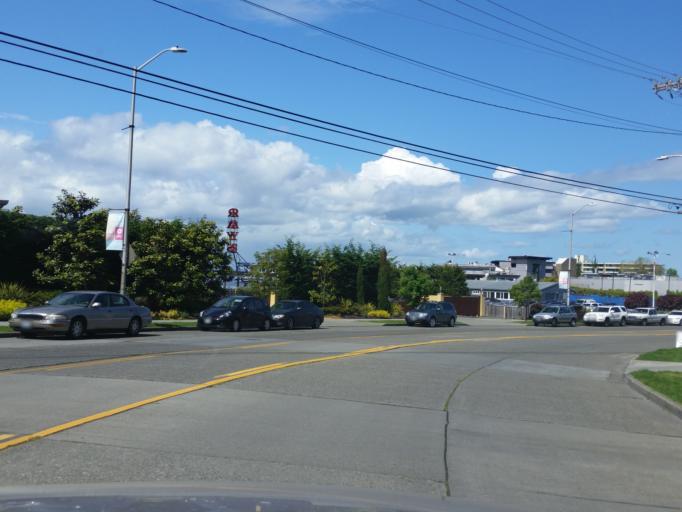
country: US
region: Washington
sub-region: King County
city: Seattle
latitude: 47.6724
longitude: -122.4060
